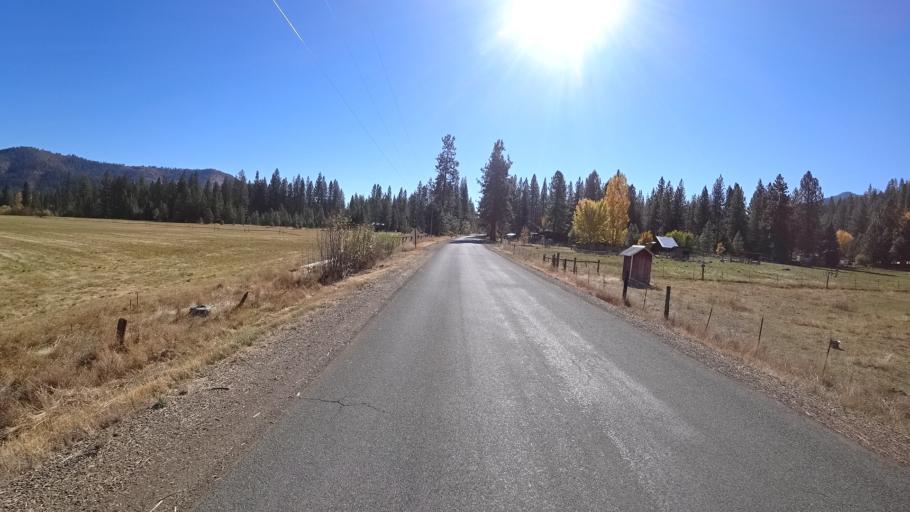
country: US
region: California
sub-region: Siskiyou County
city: Yreka
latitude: 41.6062
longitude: -122.9770
